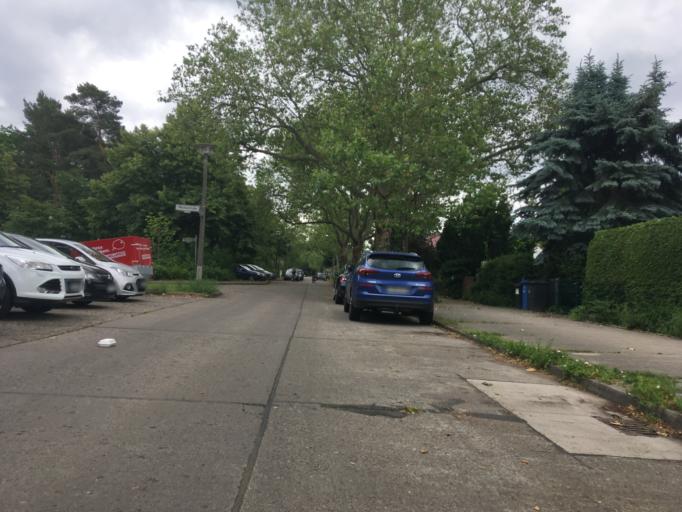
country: DE
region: Berlin
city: Friedrichshagen
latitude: 52.4532
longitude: 13.6355
